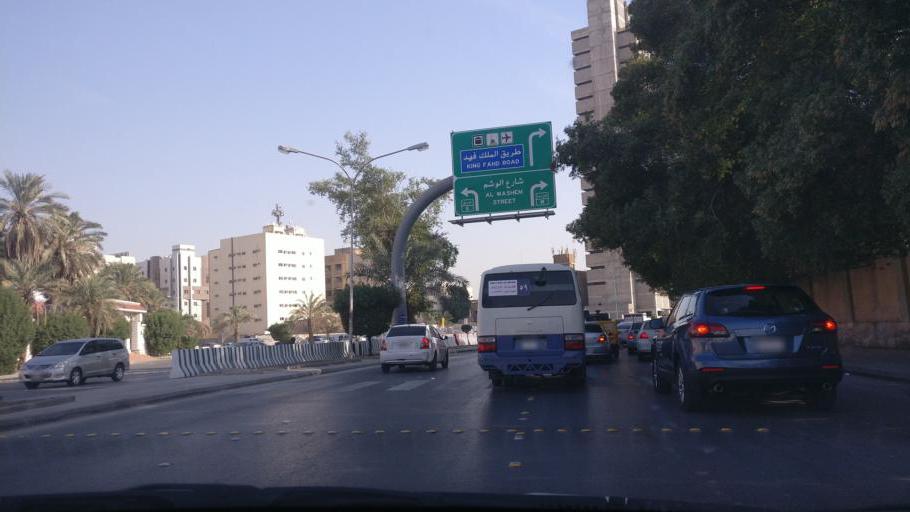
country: SA
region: Ar Riyad
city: Riyadh
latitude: 24.6548
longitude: 46.7101
